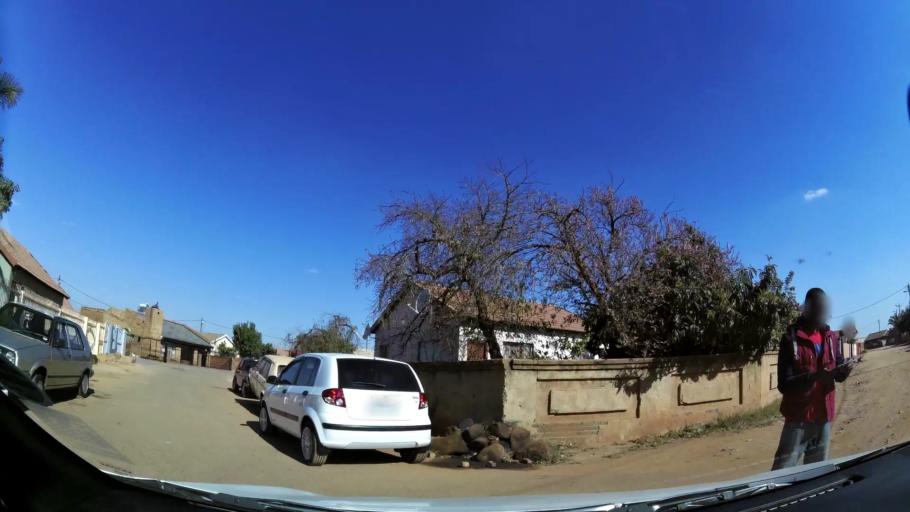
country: ZA
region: Gauteng
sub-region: City of Tshwane Metropolitan Municipality
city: Cullinan
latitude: -25.7090
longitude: 28.3928
